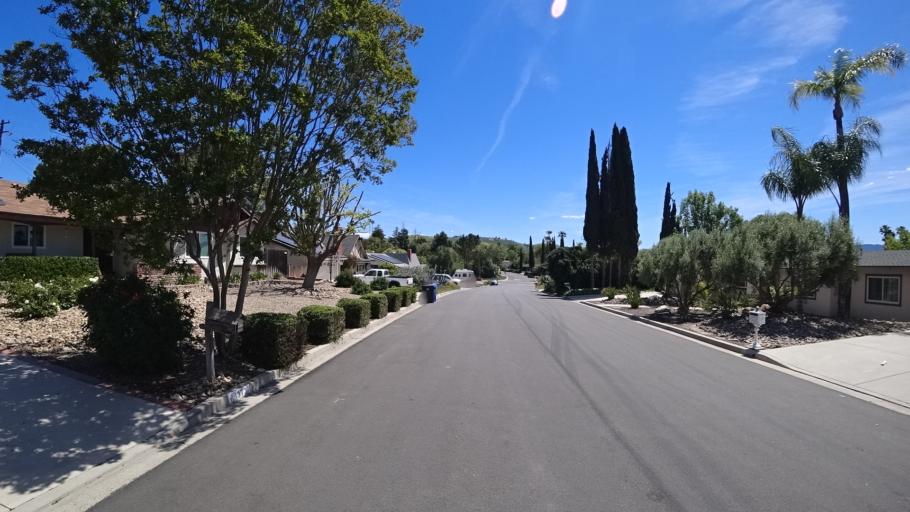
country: US
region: California
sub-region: Ventura County
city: Thousand Oaks
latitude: 34.2147
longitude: -118.8543
